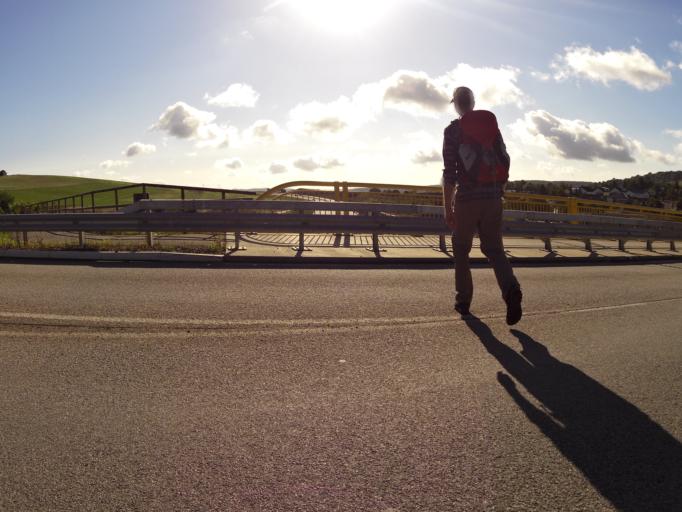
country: DE
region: Rheinland-Pfalz
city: Waldbockelheim
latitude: 49.8204
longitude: 7.7194
